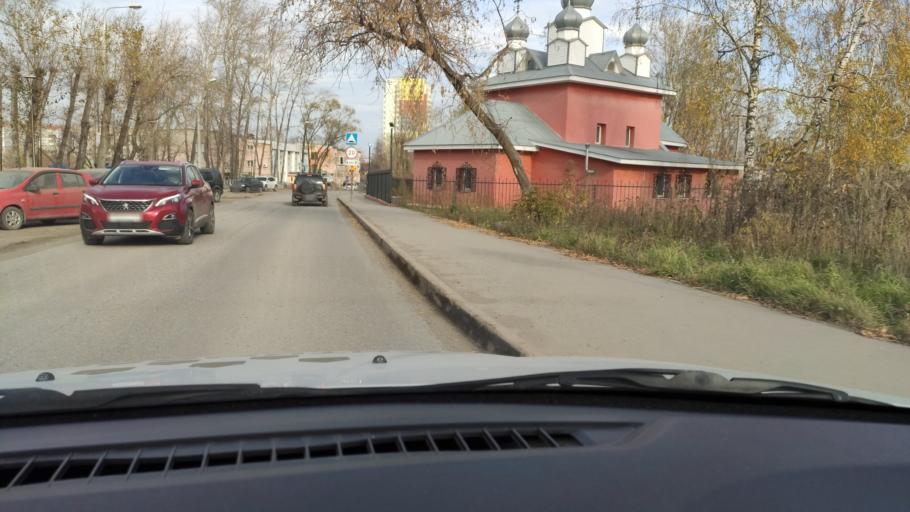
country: RU
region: Perm
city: Froly
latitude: 57.9672
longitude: 56.2735
